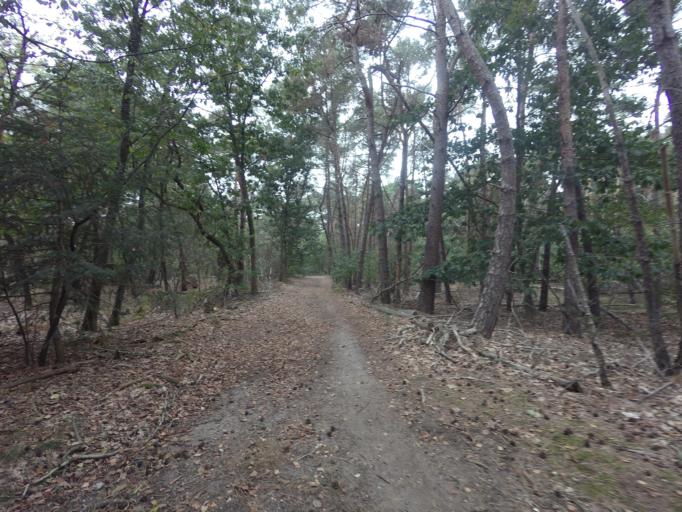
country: NL
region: North Brabant
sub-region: Gemeente Landerd
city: Schaijk
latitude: 51.7091
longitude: 5.6402
